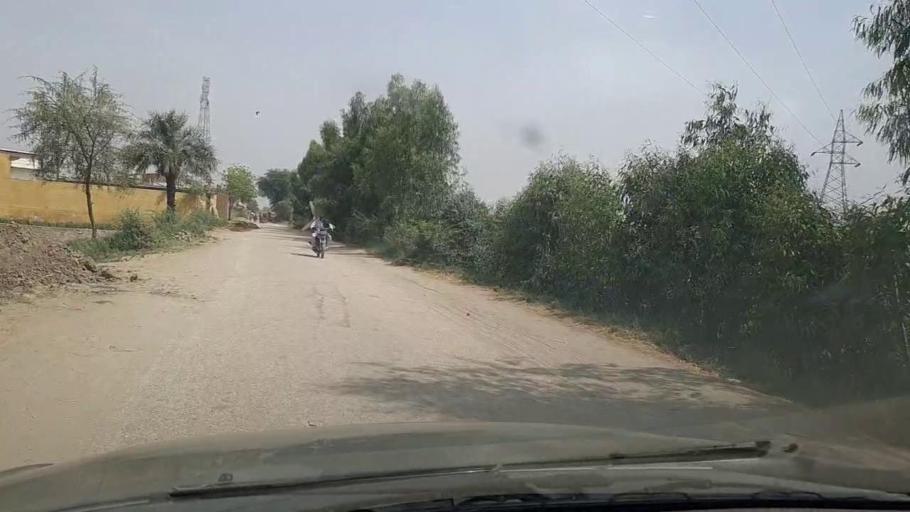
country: PK
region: Sindh
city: Shikarpur
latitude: 27.9302
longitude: 68.6604
